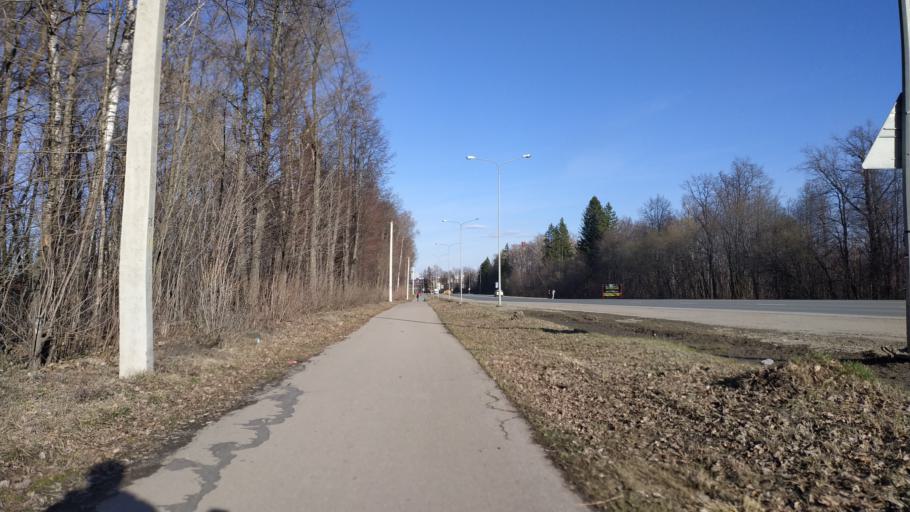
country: RU
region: Chuvashia
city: Novyye Lapsary
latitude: 56.1305
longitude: 47.1527
